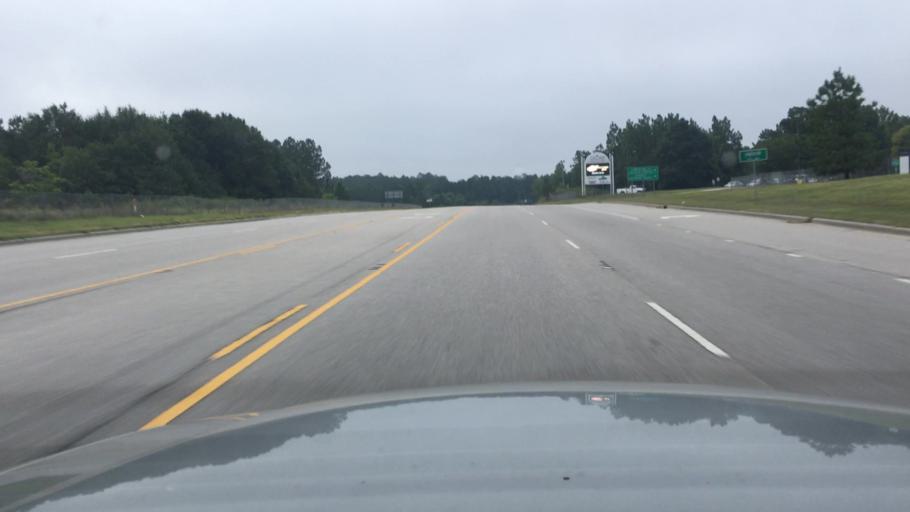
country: US
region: North Carolina
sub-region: Cumberland County
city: Fayetteville
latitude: 35.0189
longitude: -78.8914
